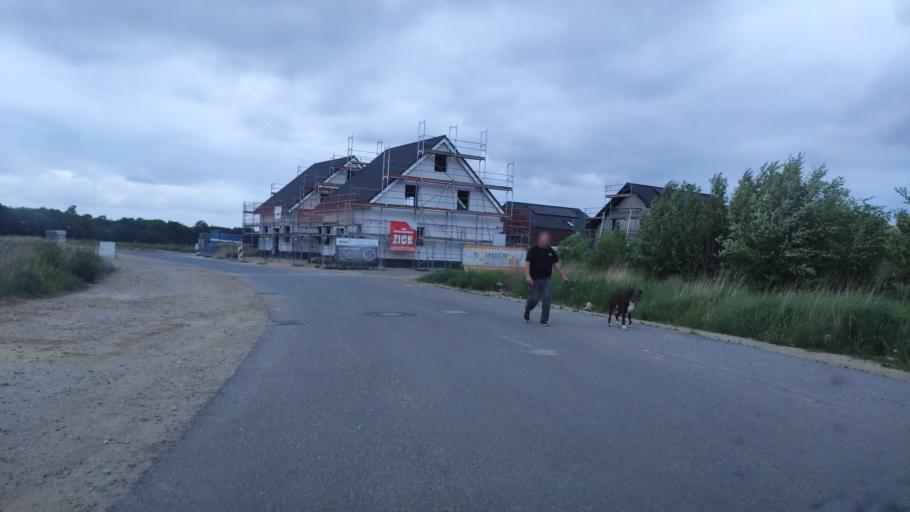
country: DE
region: North Rhine-Westphalia
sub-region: Regierungsbezirk Dusseldorf
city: Neuss
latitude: 51.1697
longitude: 6.6649
